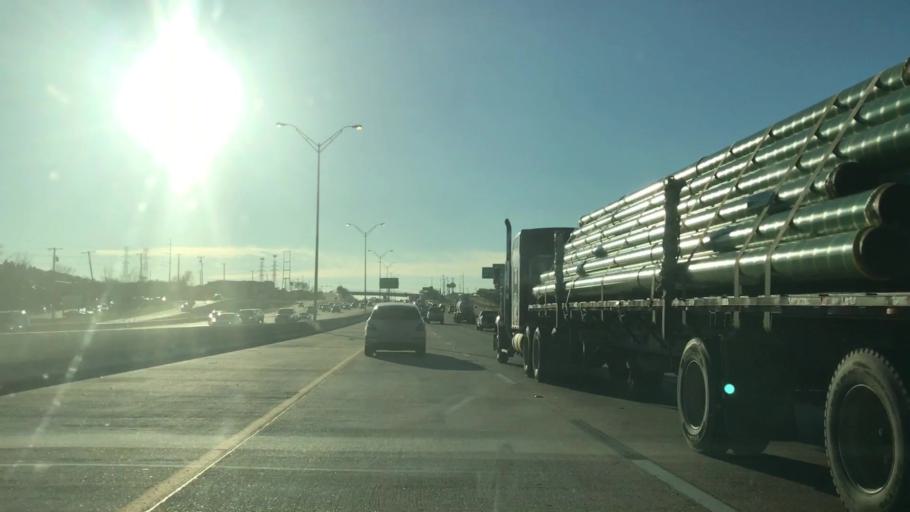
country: US
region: Texas
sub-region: Dallas County
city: Sunnyvale
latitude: 32.8365
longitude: -96.6049
